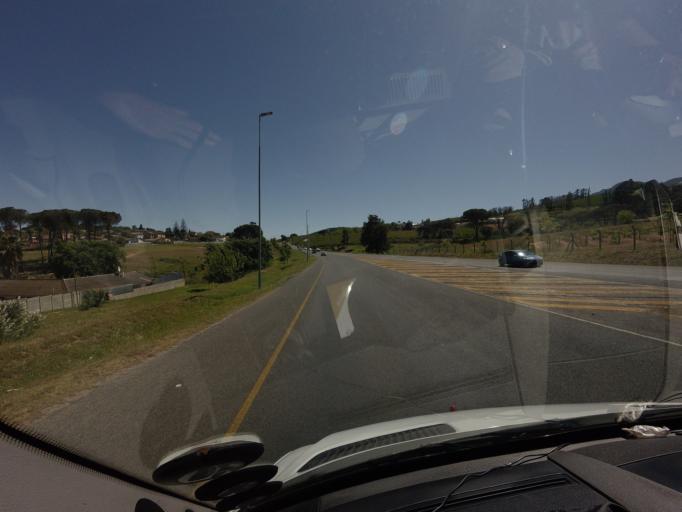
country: ZA
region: Western Cape
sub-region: Cape Winelands District Municipality
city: Stellenbosch
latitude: -33.9102
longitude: 18.8595
